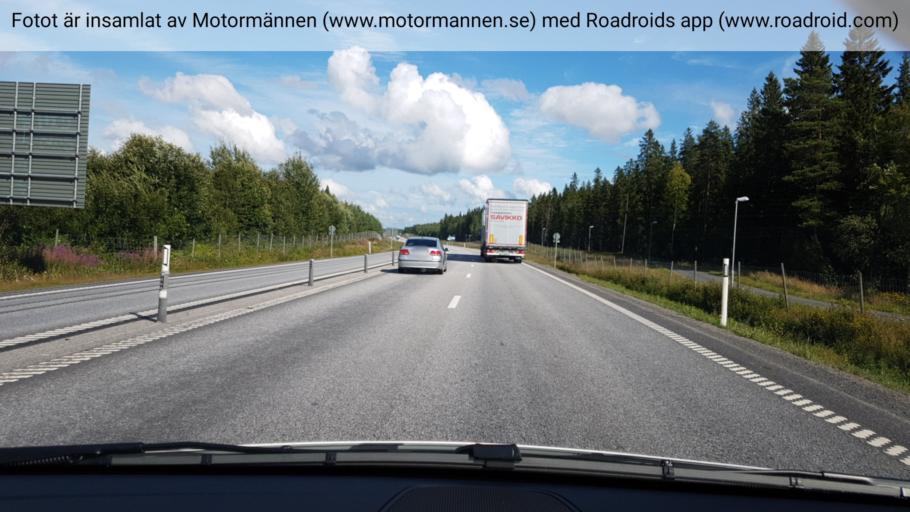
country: SE
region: Vaesterbotten
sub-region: Umea Kommun
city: Ersmark
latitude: 63.8476
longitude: 20.3479
